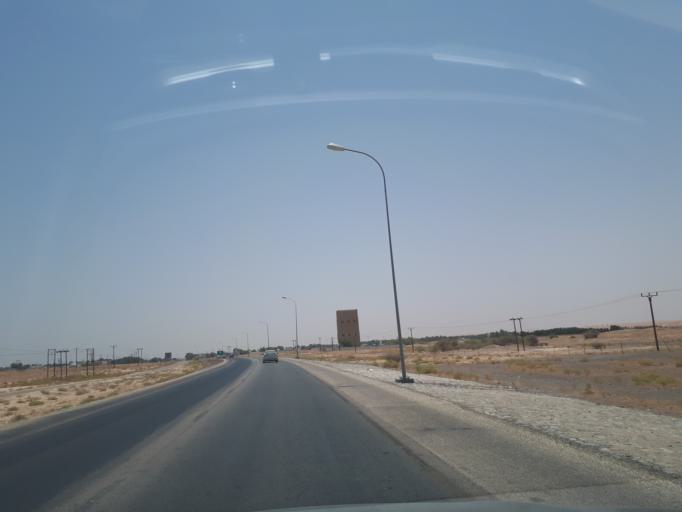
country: OM
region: Ash Sharqiyah
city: Al Qabil
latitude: 22.5115
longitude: 58.7395
